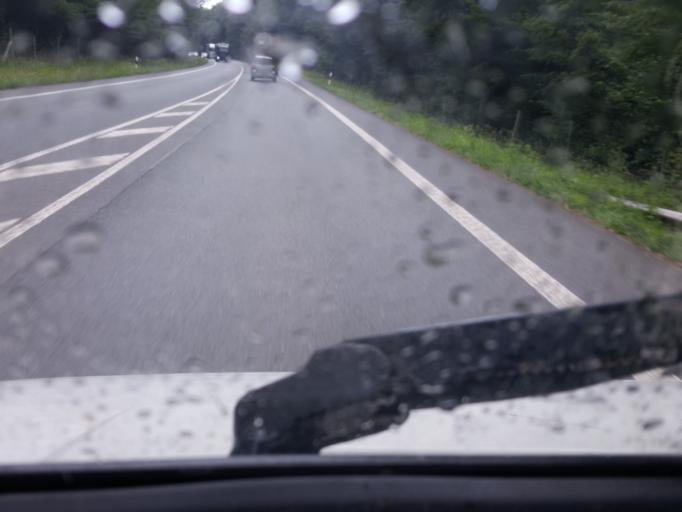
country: DE
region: North Rhine-Westphalia
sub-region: Regierungsbezirk Detmold
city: Petershagen
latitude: 52.3584
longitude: 8.9575
